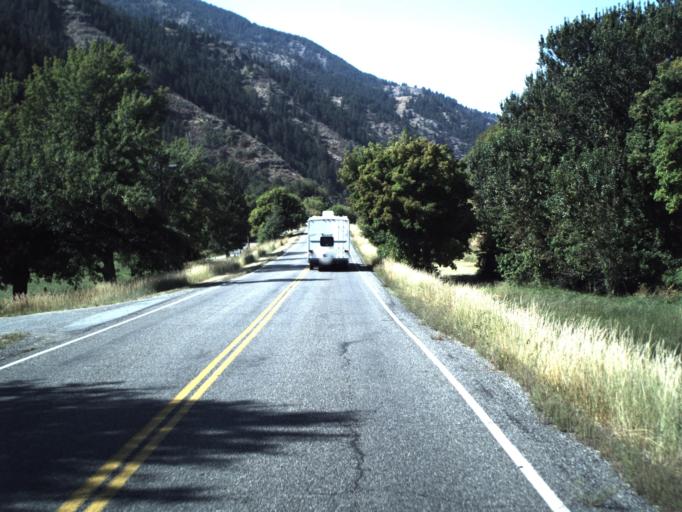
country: US
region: Utah
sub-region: Cache County
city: Millville
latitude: 41.6229
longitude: -111.7401
